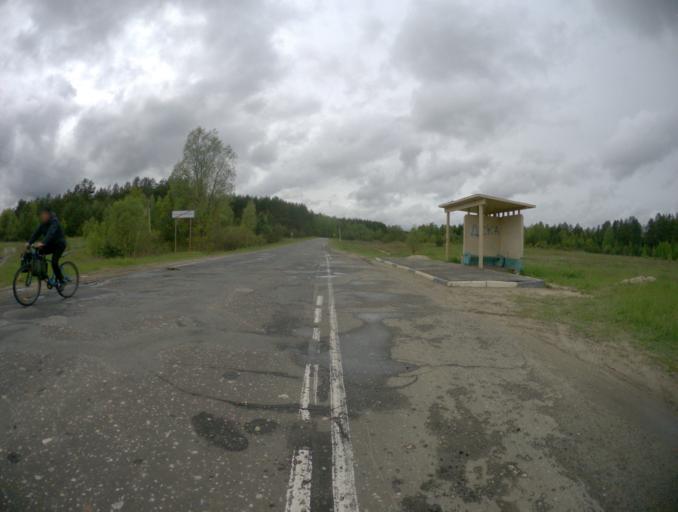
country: RU
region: Vladimir
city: Velikodvorskiy
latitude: 55.3882
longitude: 40.7395
